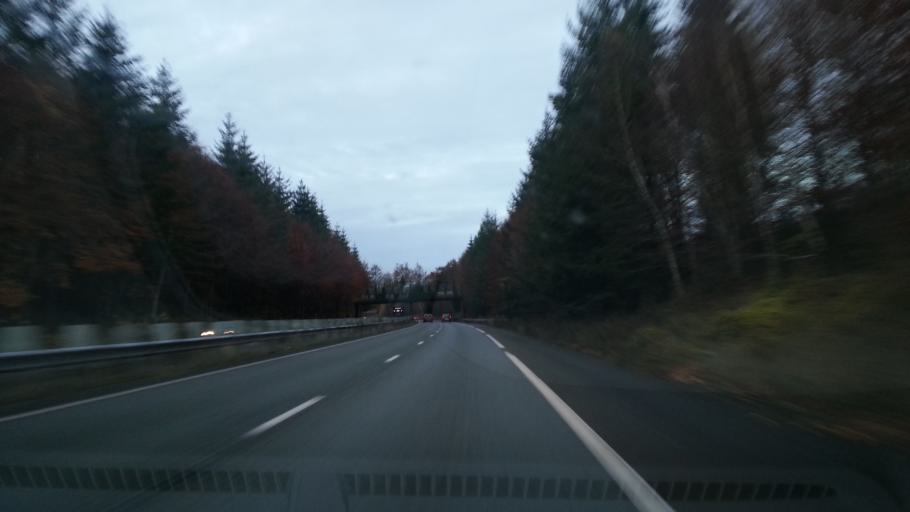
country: FR
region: Picardie
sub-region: Departement de l'Oise
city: Agnetz
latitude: 49.4040
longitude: 2.3672
